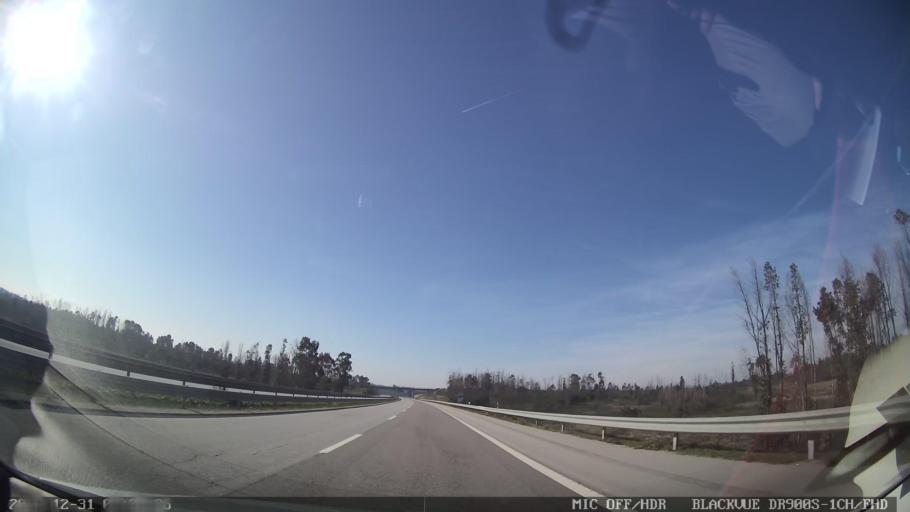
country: PT
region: Santarem
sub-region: Macao
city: Macao
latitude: 39.5344
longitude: -7.9360
